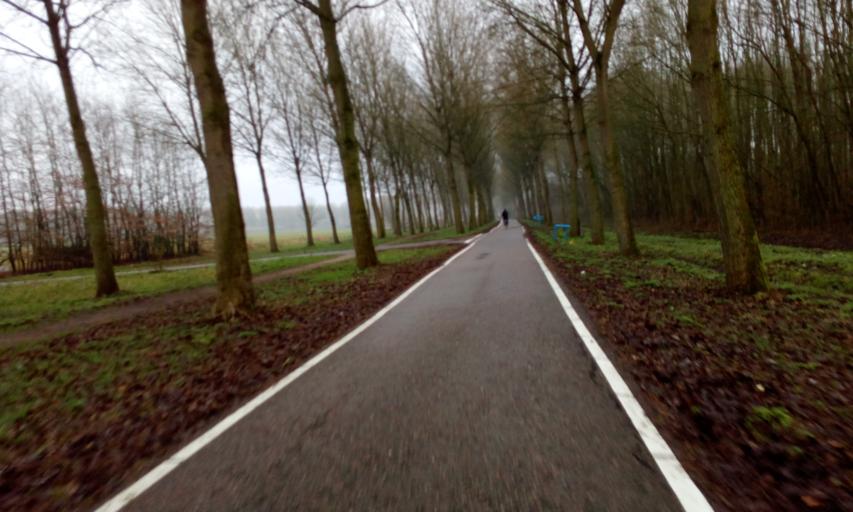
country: NL
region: South Holland
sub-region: Gemeente Den Haag
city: Ypenburg
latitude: 52.0257
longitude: 4.3887
